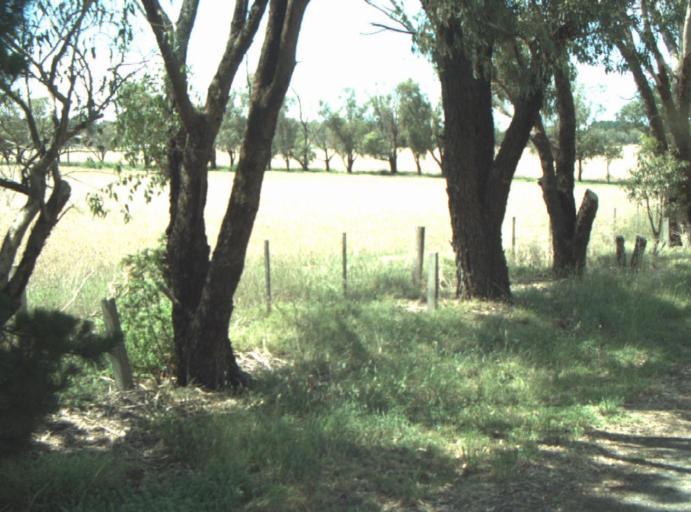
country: AU
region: Victoria
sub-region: Greater Geelong
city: Leopold
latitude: -38.1668
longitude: 144.4726
